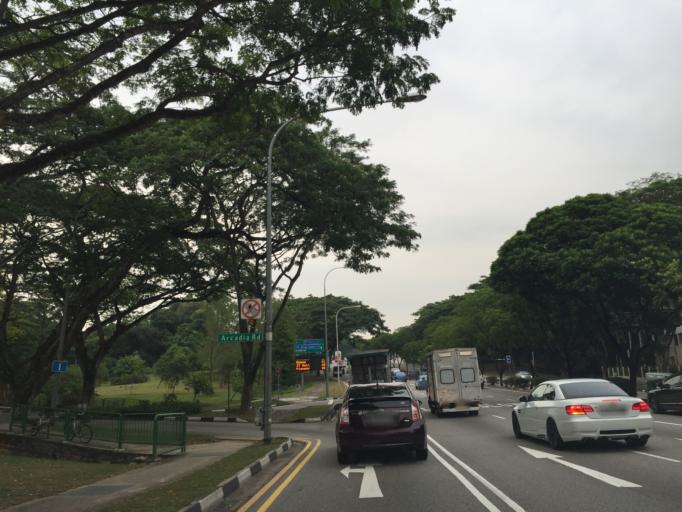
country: SG
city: Singapore
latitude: 1.3302
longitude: 103.8149
